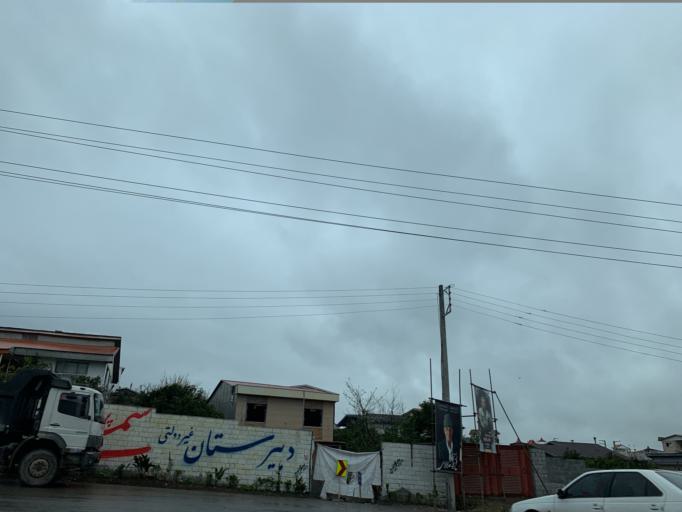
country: IR
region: Mazandaran
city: Amol
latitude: 36.4064
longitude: 52.3476
